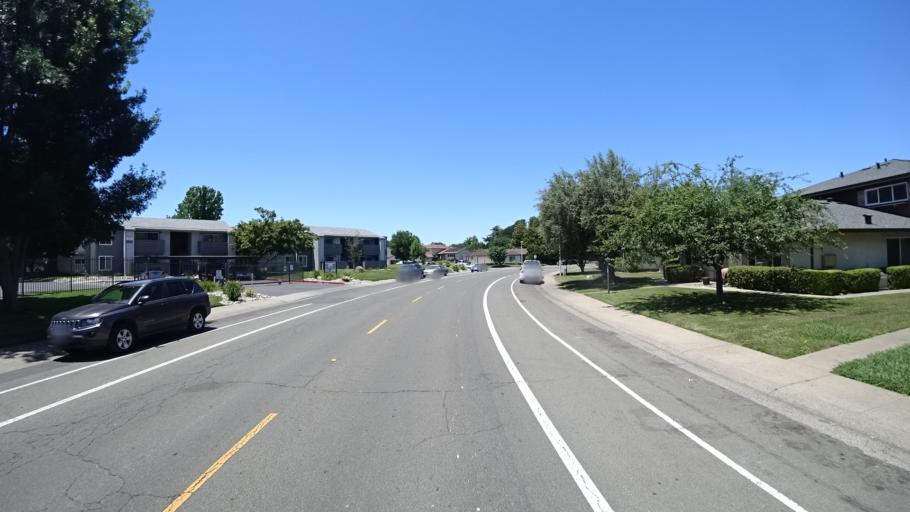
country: US
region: California
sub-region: Sacramento County
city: Rosemont
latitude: 38.5511
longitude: -121.3921
